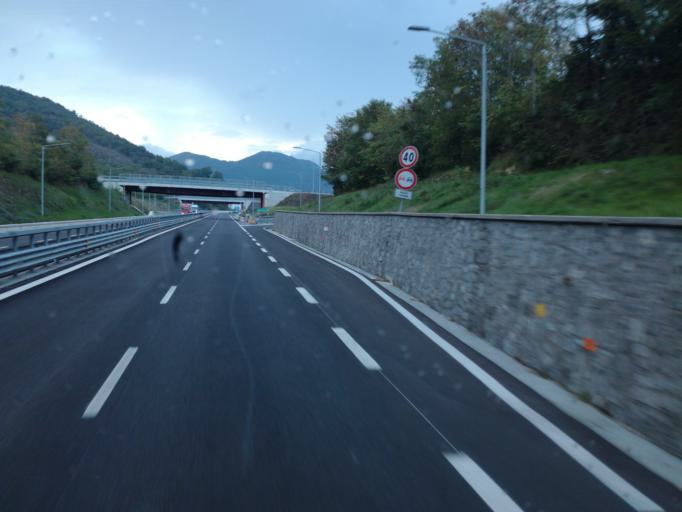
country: IT
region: Calabria
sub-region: Provincia di Cosenza
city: Laino Borgo
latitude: 39.9648
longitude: 15.9327
